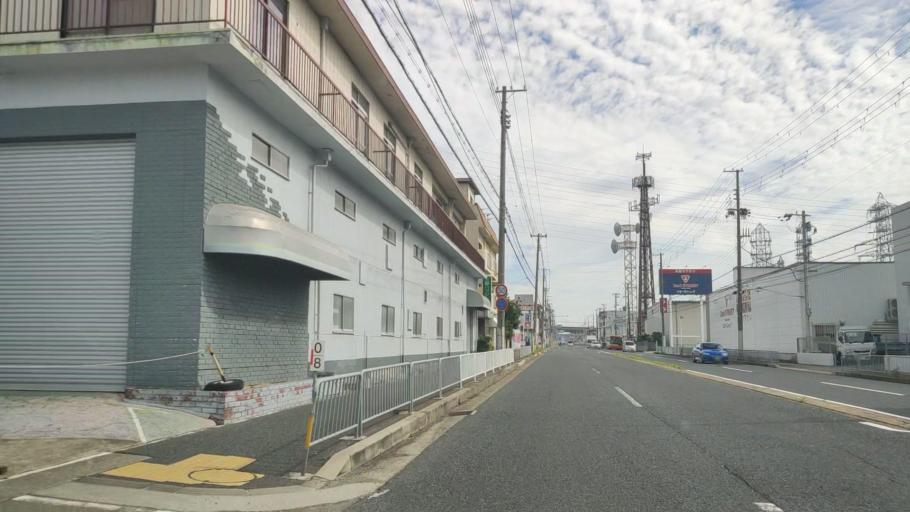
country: JP
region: Hyogo
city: Akashi
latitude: 34.6607
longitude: 134.9777
